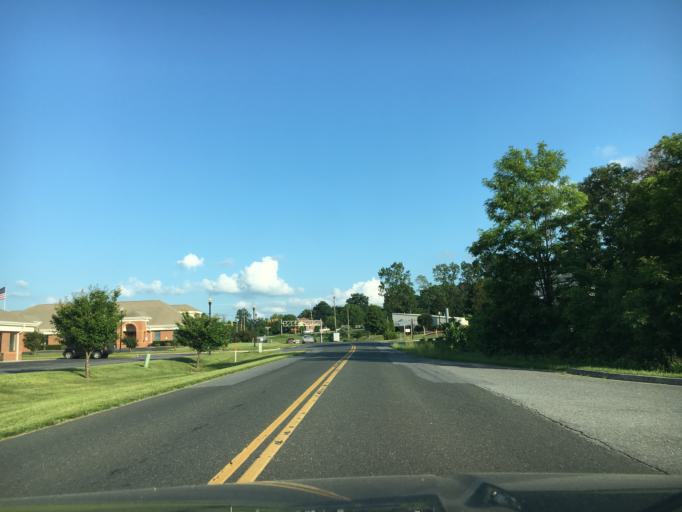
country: US
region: Virginia
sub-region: Bedford County
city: Forest
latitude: 37.3716
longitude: -79.2552
